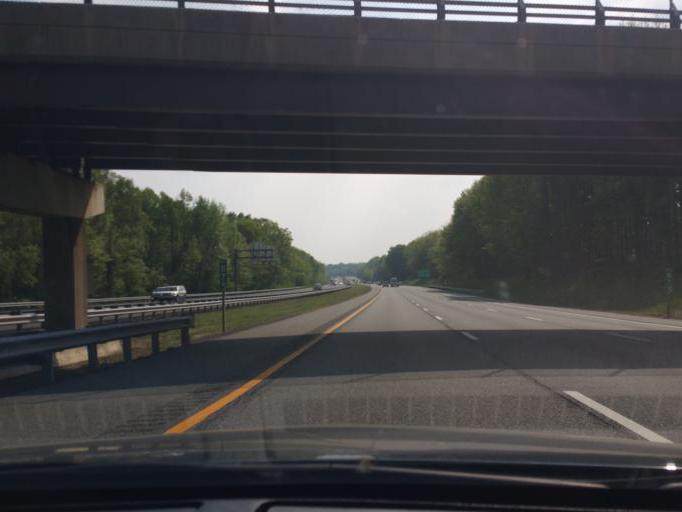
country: US
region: Maryland
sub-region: Harford County
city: Aberdeen
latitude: 39.5565
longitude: -76.1546
